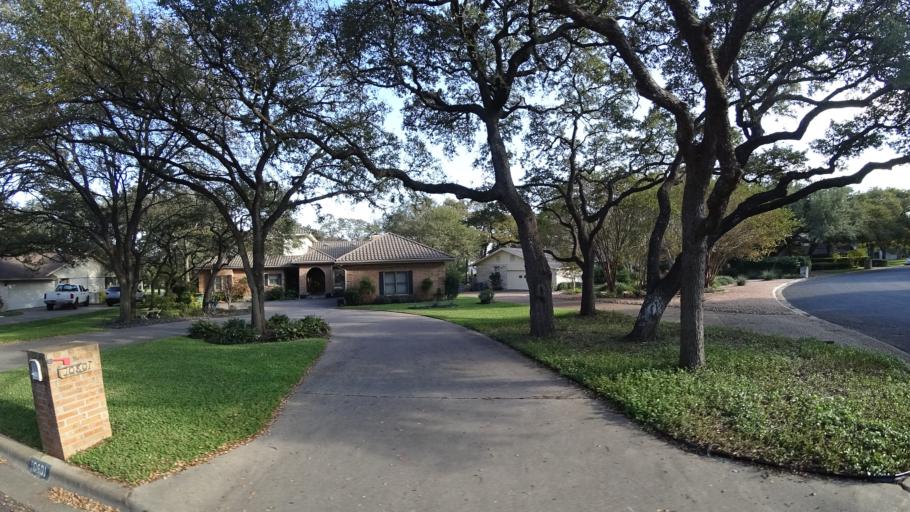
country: US
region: Texas
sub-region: Williamson County
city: Anderson Mill
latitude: 30.4338
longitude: -97.8040
